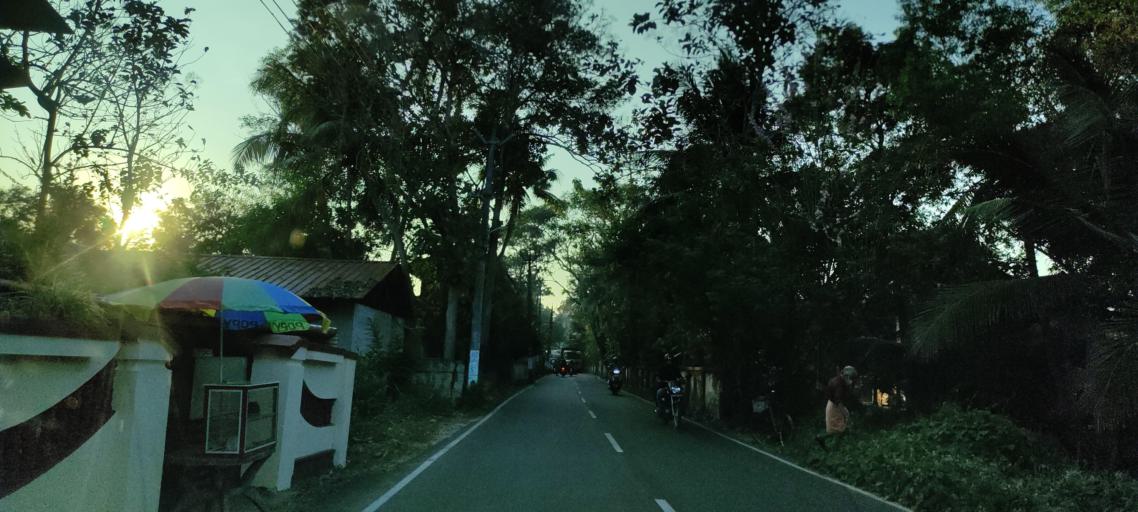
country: IN
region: Kerala
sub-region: Alappuzha
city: Alleppey
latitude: 9.5403
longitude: 76.3394
